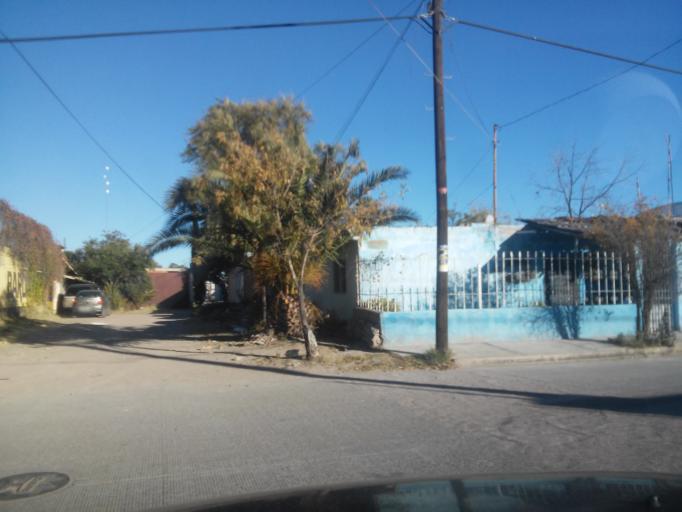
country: MX
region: Durango
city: Victoria de Durango
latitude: 24.0141
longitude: -104.6365
